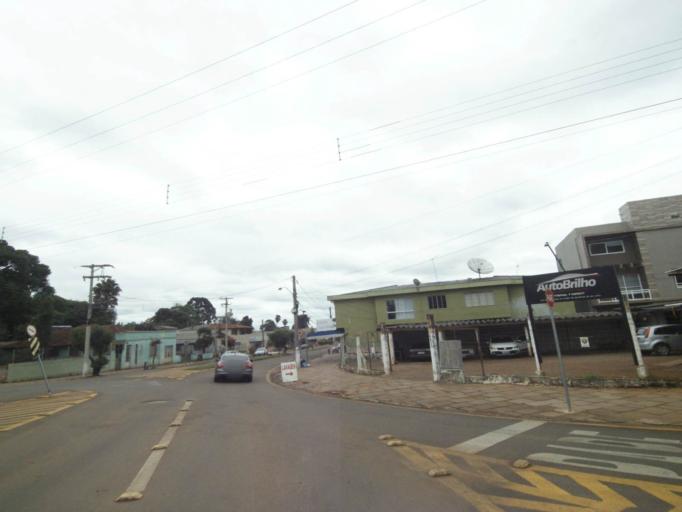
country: BR
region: Rio Grande do Sul
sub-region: Lagoa Vermelha
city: Lagoa Vermelha
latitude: -28.2095
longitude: -51.5298
